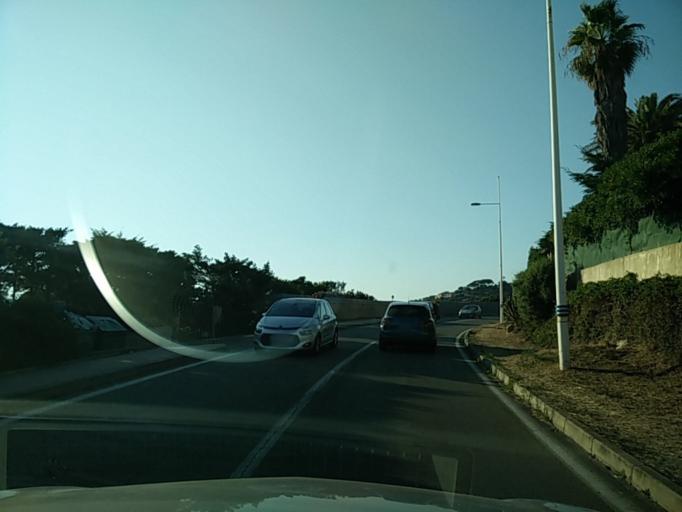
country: FR
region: Corsica
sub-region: Departement de la Corse-du-Sud
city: Pietrosella
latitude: 41.8692
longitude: 8.7874
